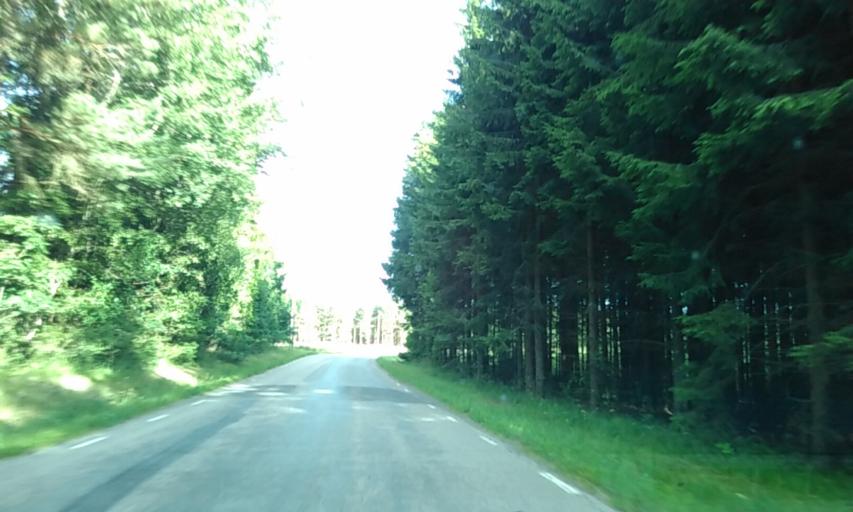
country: SE
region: Vaestra Goetaland
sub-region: Vara Kommun
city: Vara
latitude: 58.3536
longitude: 12.8733
